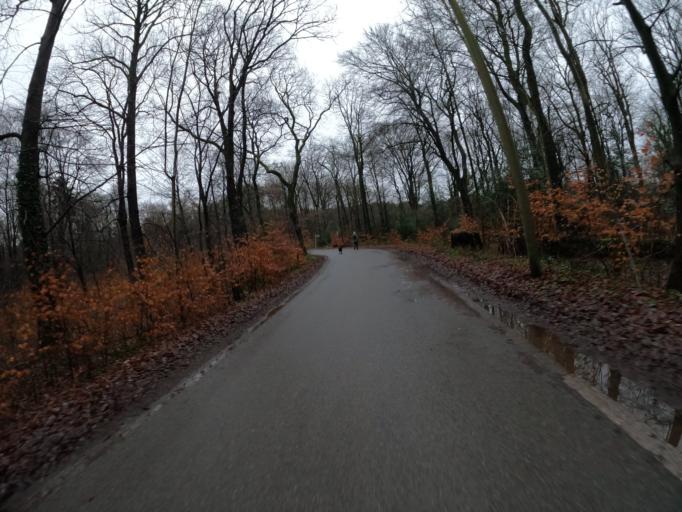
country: DE
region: North Rhine-Westphalia
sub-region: Regierungsbezirk Dusseldorf
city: Wuppertal
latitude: 51.2362
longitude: 7.1280
